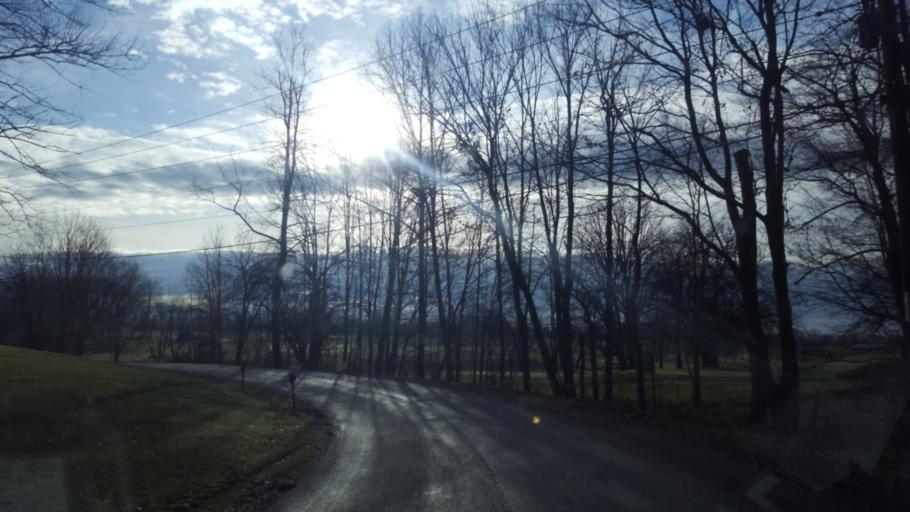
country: US
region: Ohio
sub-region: Richland County
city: Lexington
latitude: 40.6449
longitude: -82.6122
